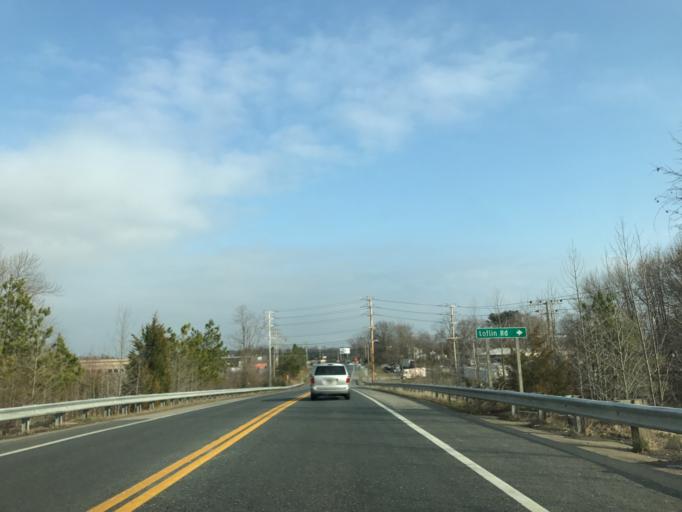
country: US
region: Maryland
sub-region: Harford County
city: Perryman
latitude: 39.4908
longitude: -76.2031
